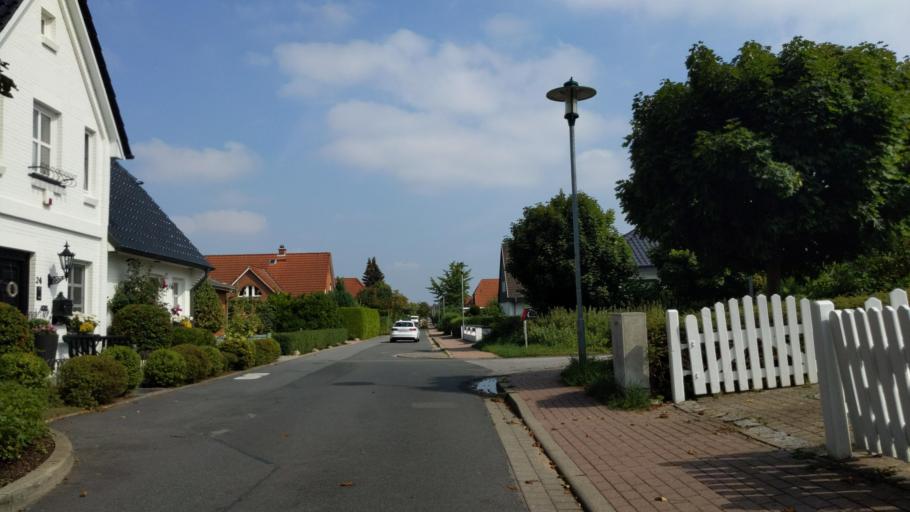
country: DE
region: Schleswig-Holstein
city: Stockelsdorf
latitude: 53.8840
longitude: 10.6356
